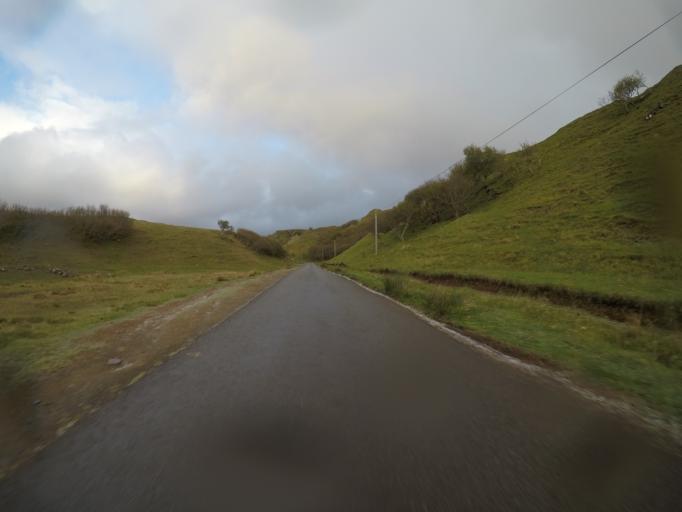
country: GB
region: Scotland
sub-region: Highland
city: Portree
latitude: 57.5844
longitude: -6.3326
